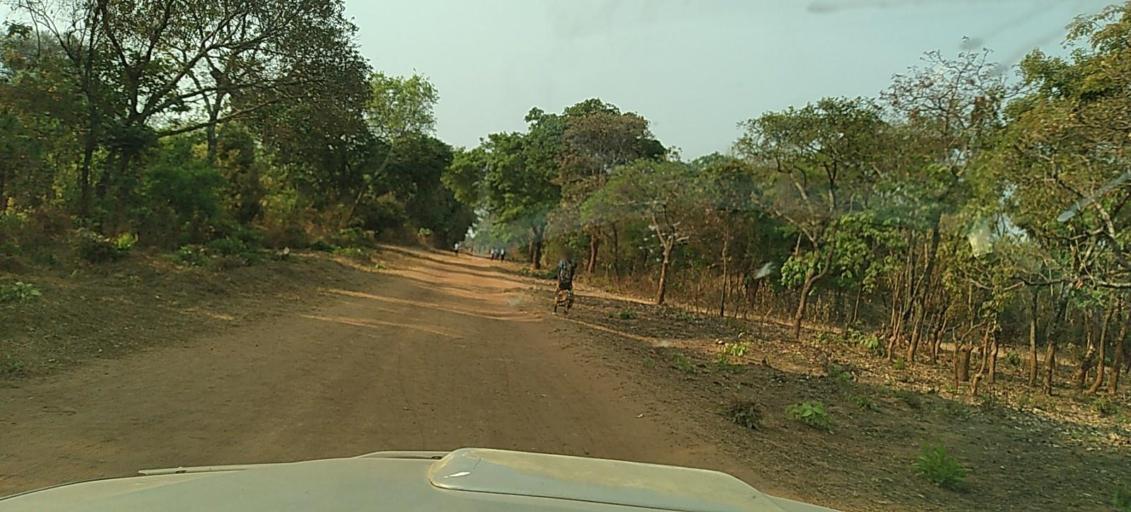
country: ZM
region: North-Western
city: Kasempa
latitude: -13.3080
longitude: 26.5528
